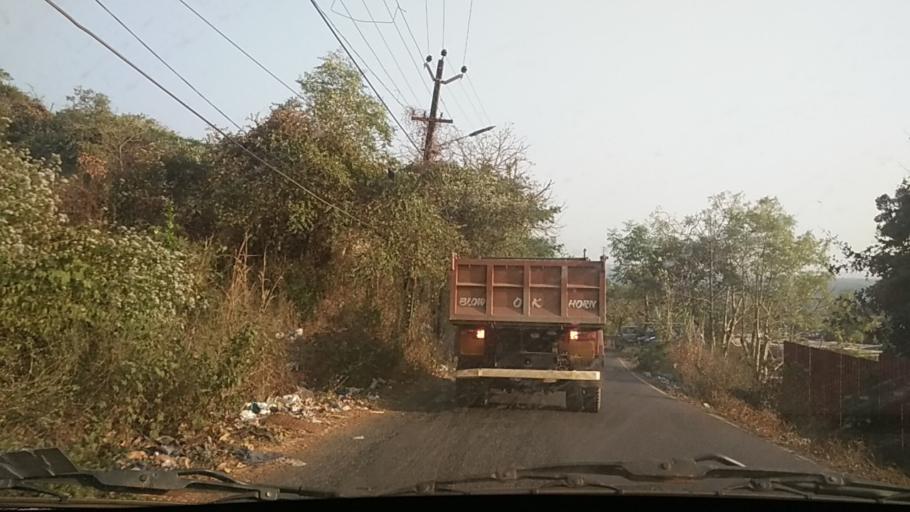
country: IN
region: Goa
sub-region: North Goa
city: Goa Velha
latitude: 15.4618
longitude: 73.8788
